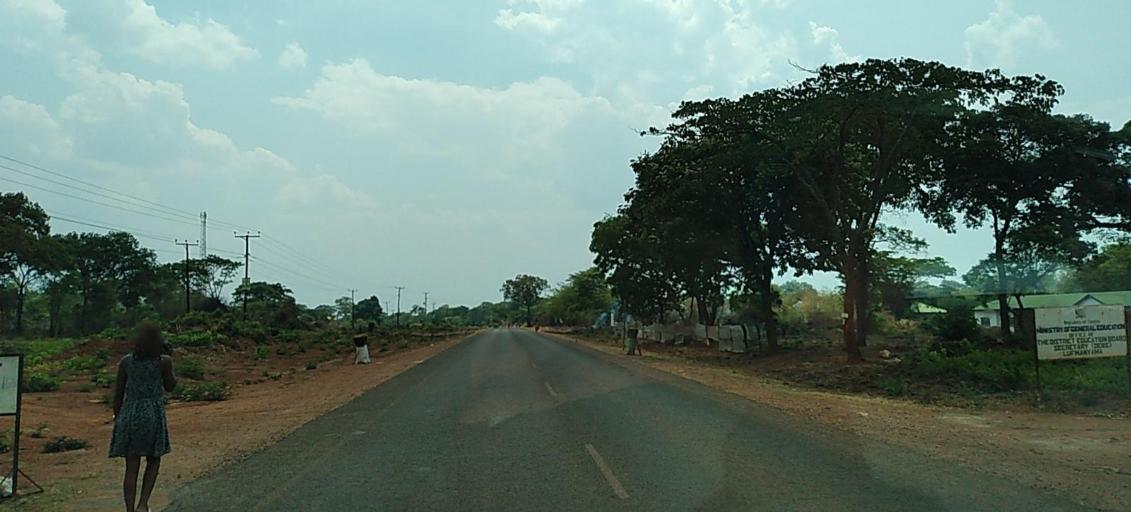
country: ZM
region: Copperbelt
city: Chingola
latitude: -12.8573
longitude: 27.6243
